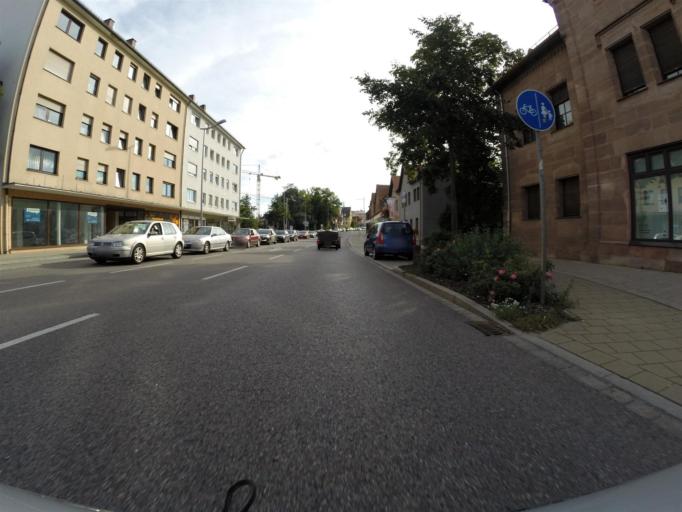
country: DE
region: Bavaria
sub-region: Regierungsbezirk Mittelfranken
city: Stein
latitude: 49.4141
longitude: 11.0152
